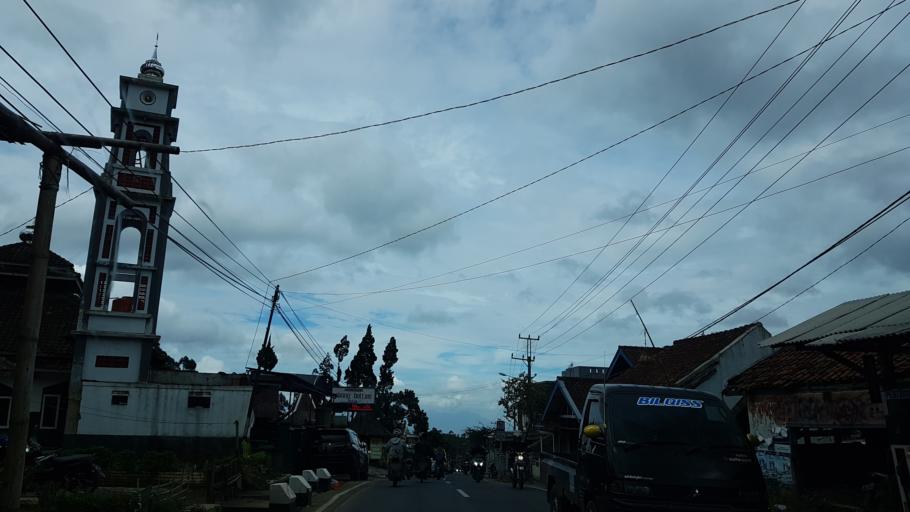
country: ID
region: West Java
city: Banjar
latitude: -7.1141
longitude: 107.4385
